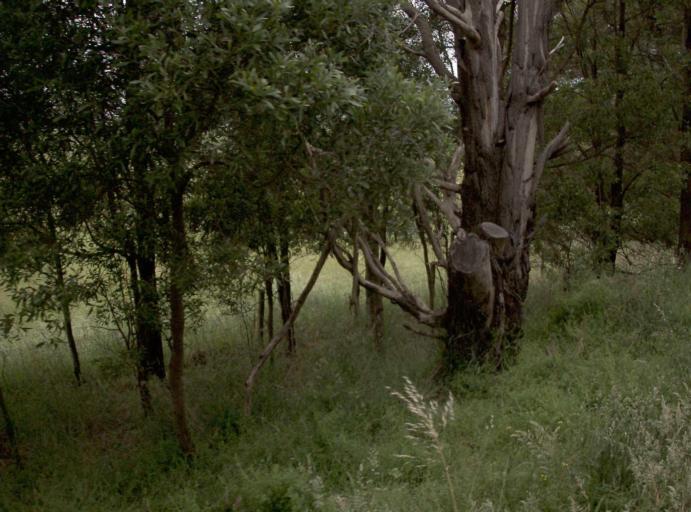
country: AU
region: Victoria
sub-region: Bass Coast
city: North Wonthaggi
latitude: -38.4947
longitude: 145.7350
